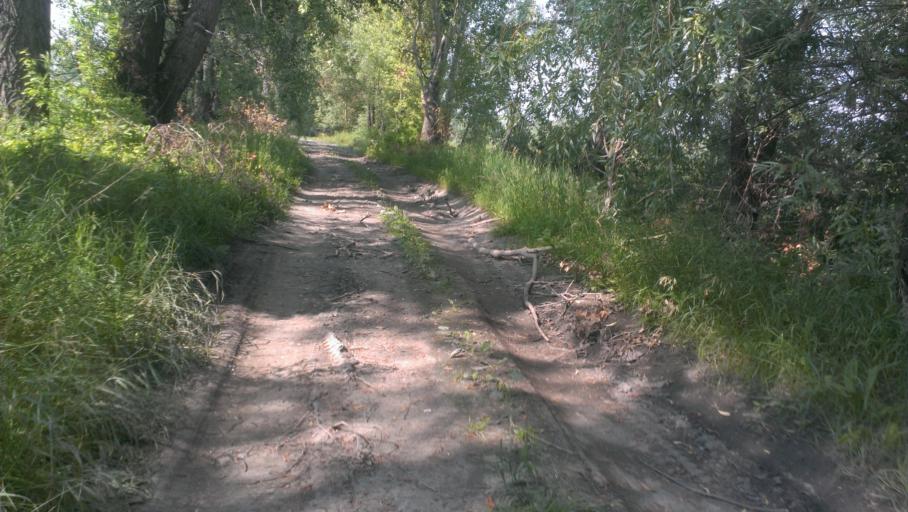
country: RU
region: Altai Krai
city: Novoaltaysk
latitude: 53.3751
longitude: 83.8570
